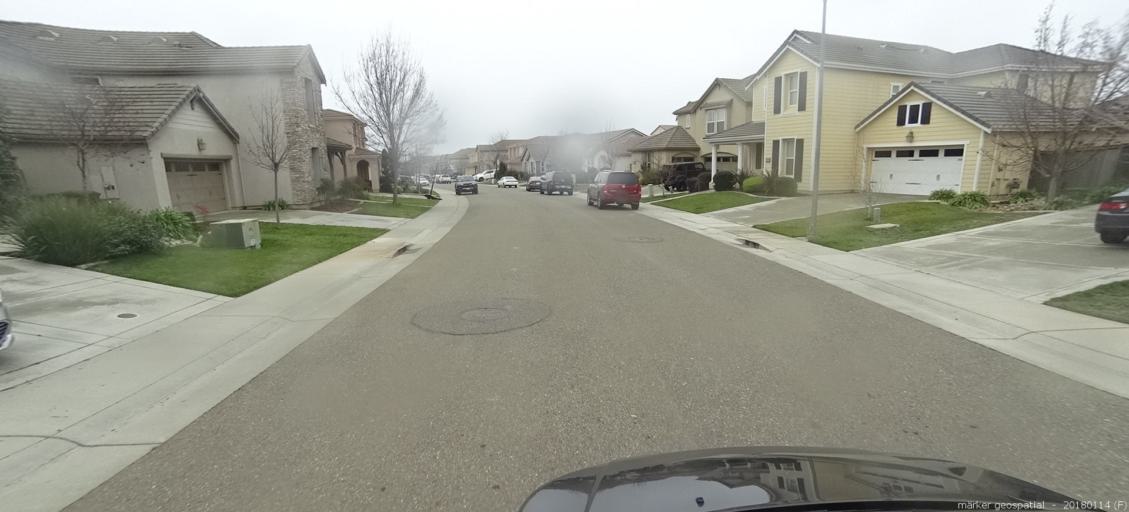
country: US
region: California
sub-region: Sacramento County
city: Rancho Cordova
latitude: 38.5279
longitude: -121.2333
